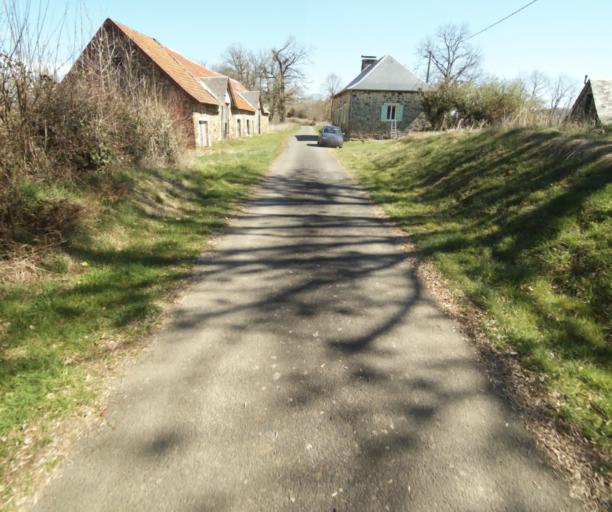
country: FR
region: Limousin
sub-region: Departement de la Correze
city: Chamboulive
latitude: 45.4484
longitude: 1.6916
